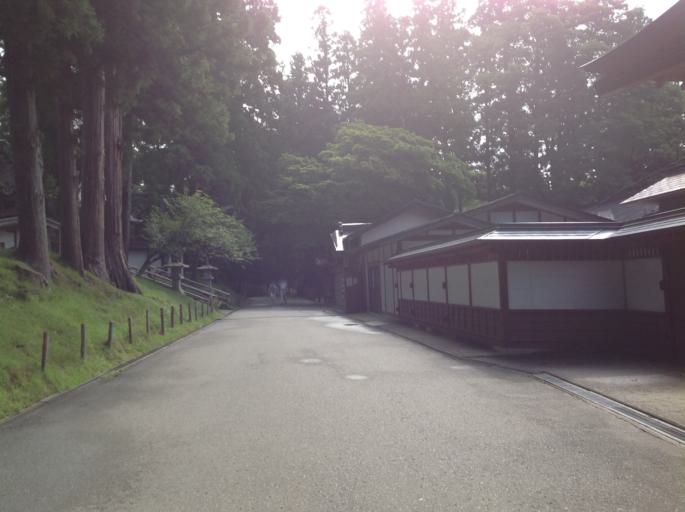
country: JP
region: Iwate
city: Ichinoseki
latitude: 39.0013
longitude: 141.1020
